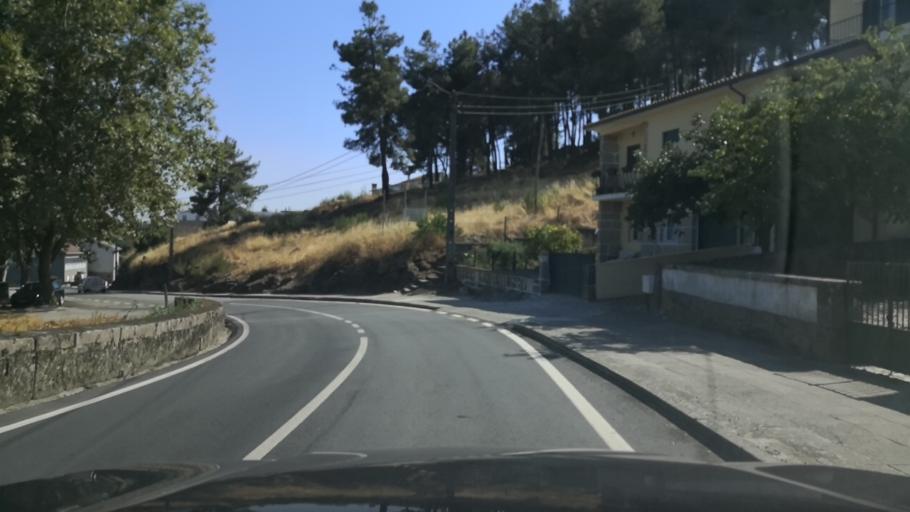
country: PT
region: Vila Real
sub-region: Sabrosa
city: Sabrosa
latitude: 41.2806
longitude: -7.4765
